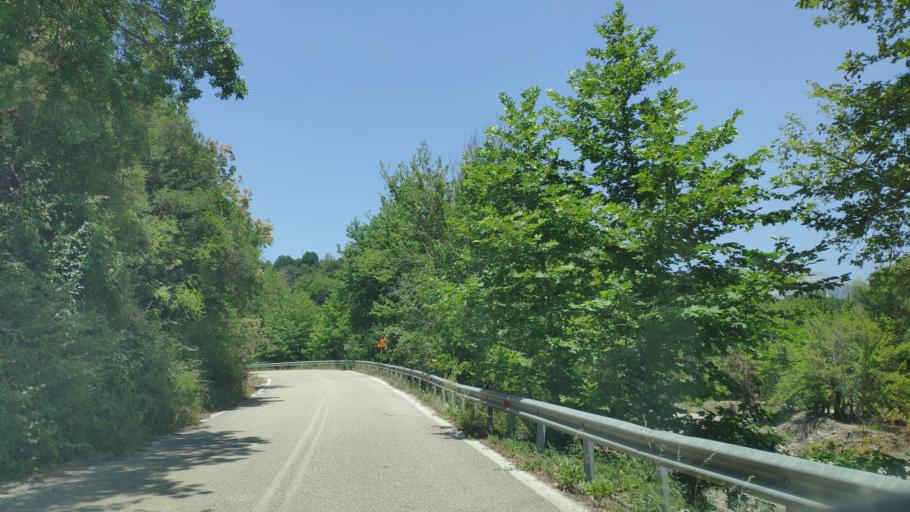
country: GR
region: Epirus
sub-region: Nomos Artas
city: Ano Kalentini
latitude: 39.2105
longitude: 21.3475
